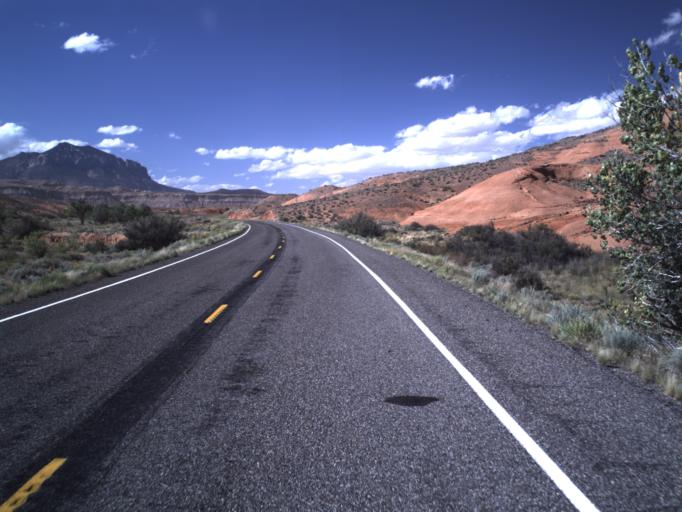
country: US
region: Utah
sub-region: Wayne County
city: Loa
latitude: 38.0538
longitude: -110.5885
